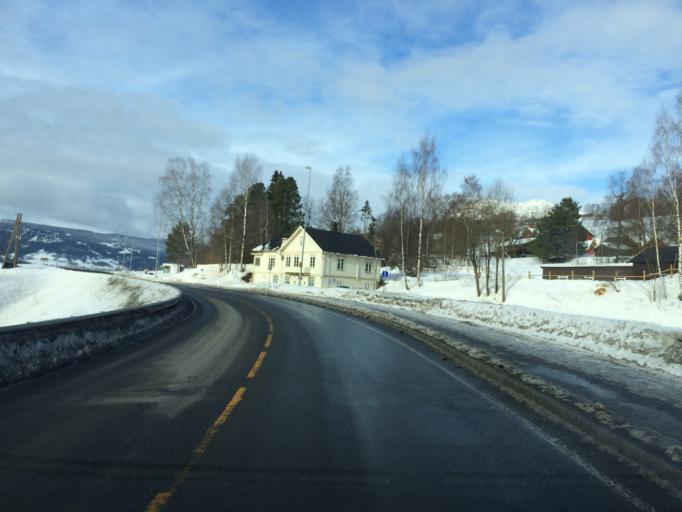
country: NO
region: Oppland
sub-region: Gausdal
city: Segalstad bru
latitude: 61.2189
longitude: 10.2748
